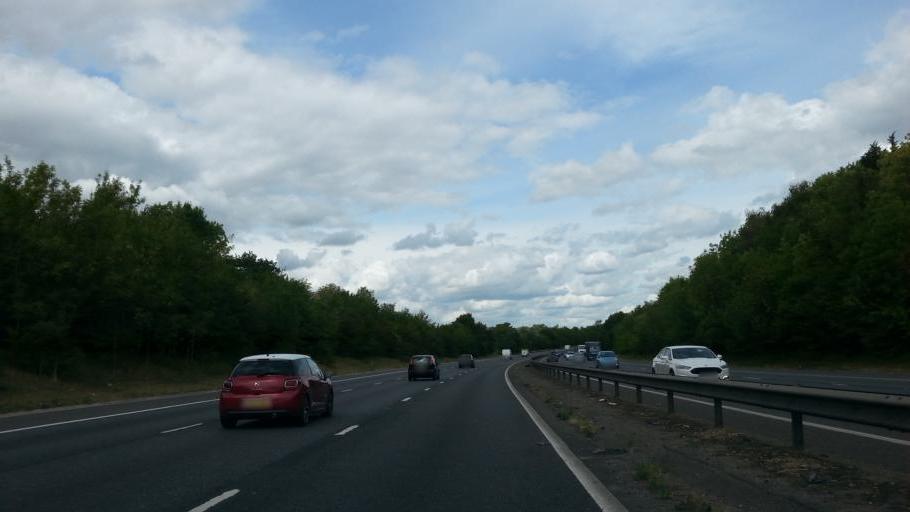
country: GB
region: England
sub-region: Hertfordshire
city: Sawbridgeworth
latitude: 51.8047
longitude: 0.1761
